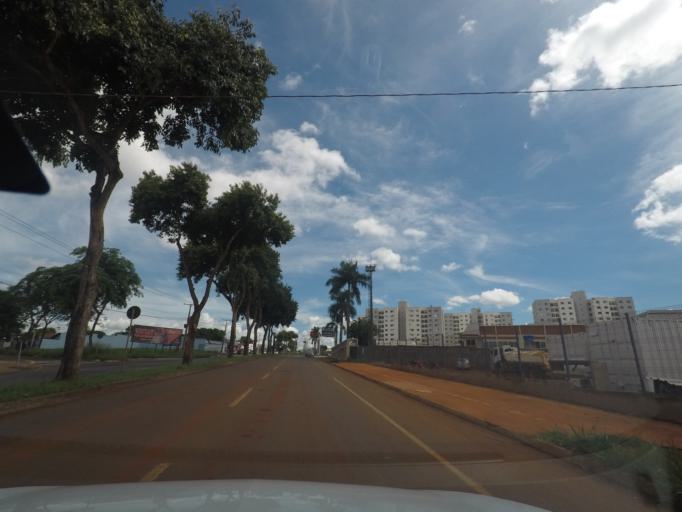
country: BR
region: Goias
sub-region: Goiania
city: Goiania
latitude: -16.7309
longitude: -49.3250
